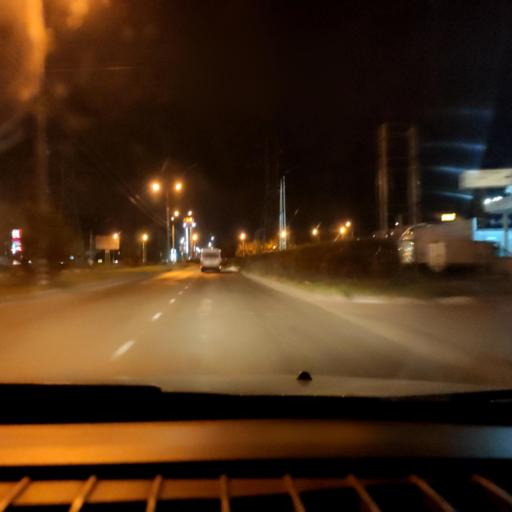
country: RU
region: Samara
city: Tol'yatti
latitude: 53.5525
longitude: 49.3182
